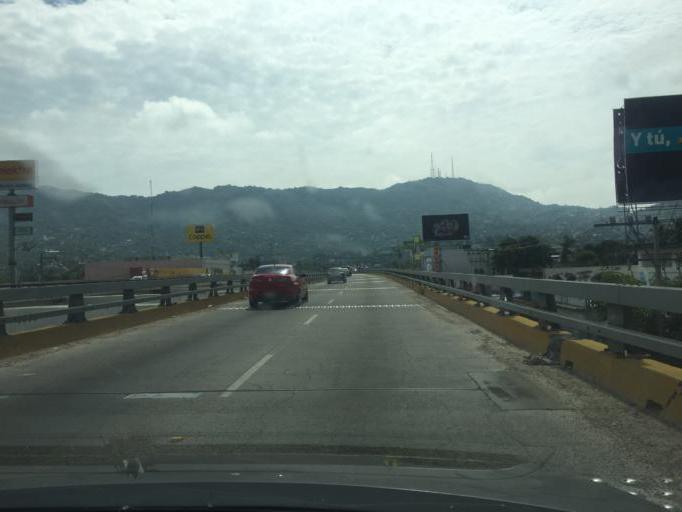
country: MX
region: Guerrero
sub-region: Acapulco de Juarez
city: Nueva Frontera
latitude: 16.8930
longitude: -99.8343
